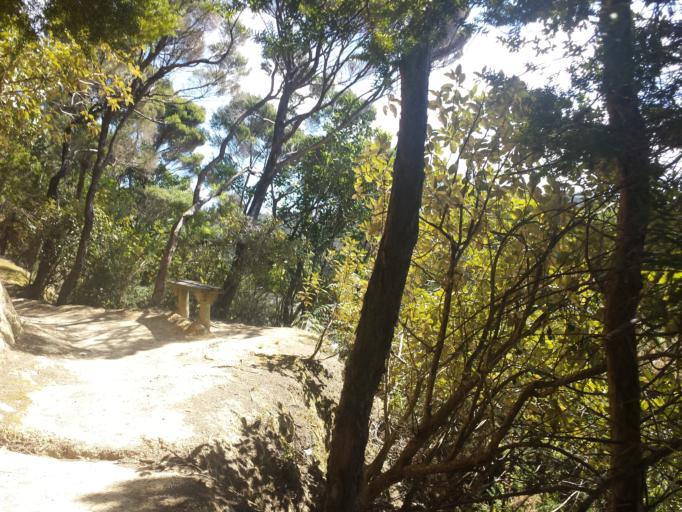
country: NZ
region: Northland
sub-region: Far North District
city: Paihia
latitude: -35.3024
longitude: 174.1060
